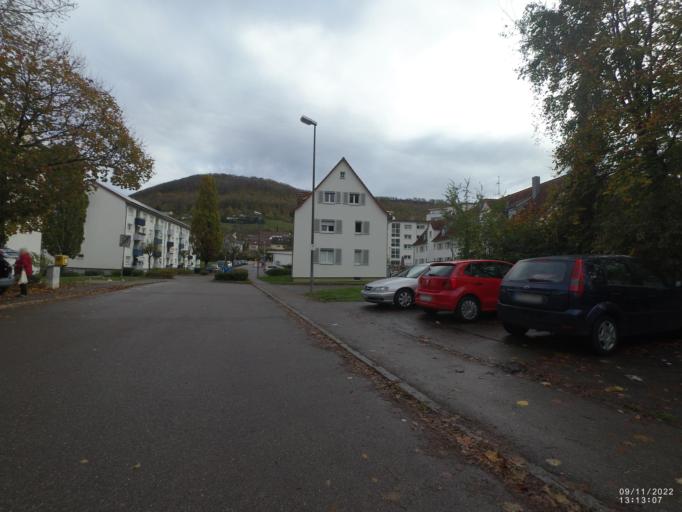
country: DE
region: Baden-Wuerttemberg
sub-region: Regierungsbezirk Stuttgart
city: Geislingen an der Steige
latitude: 48.6169
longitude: 9.8154
